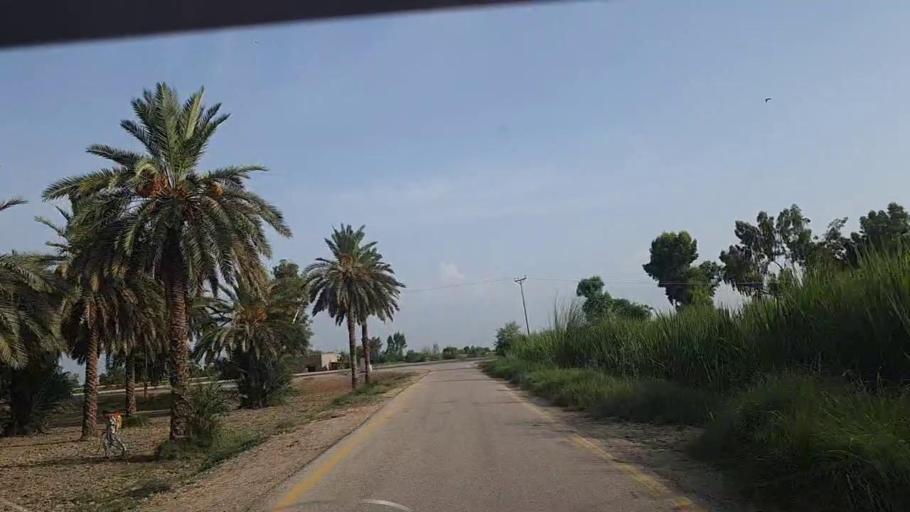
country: PK
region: Sindh
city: Adilpur
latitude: 27.9631
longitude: 69.2563
